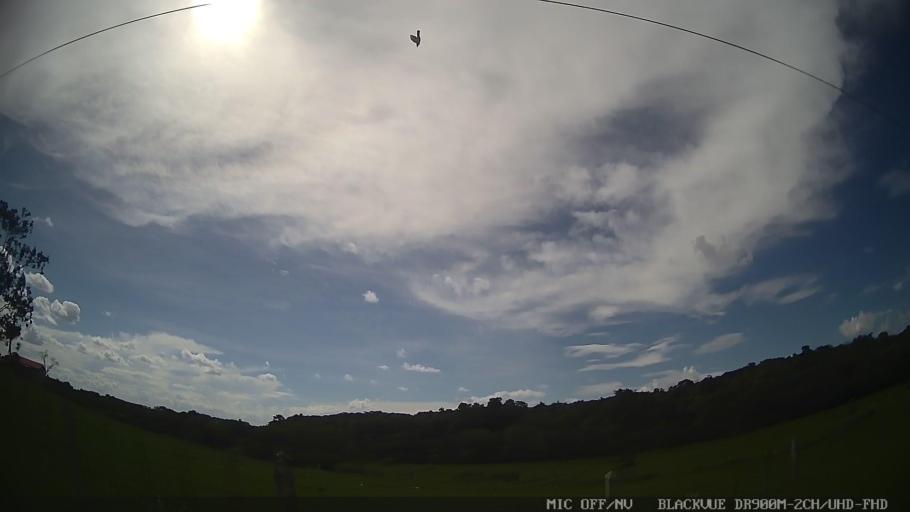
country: BR
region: Sao Paulo
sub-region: Conchas
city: Conchas
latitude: -22.9906
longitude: -47.9968
